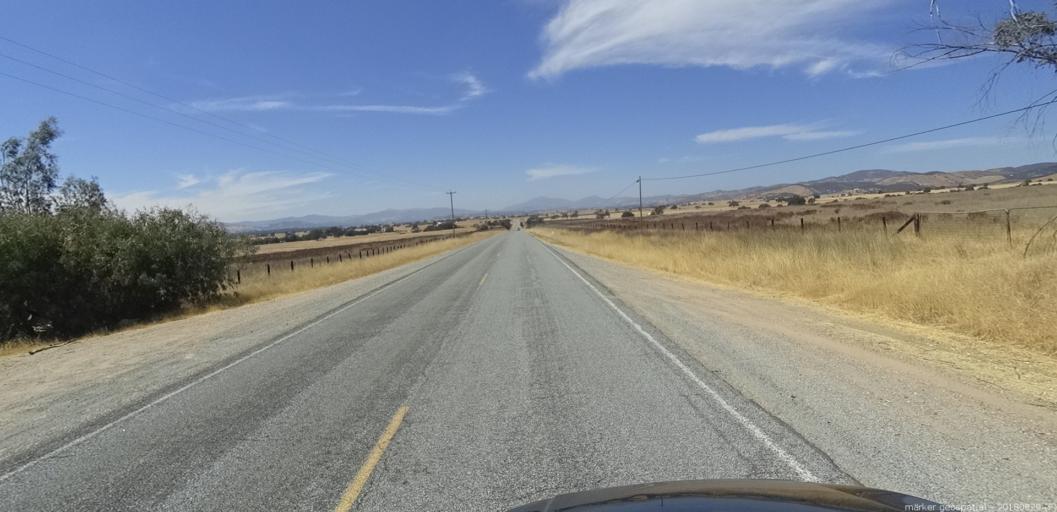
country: US
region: California
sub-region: San Luis Obispo County
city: Lake Nacimiento
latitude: 35.9259
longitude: -121.0439
